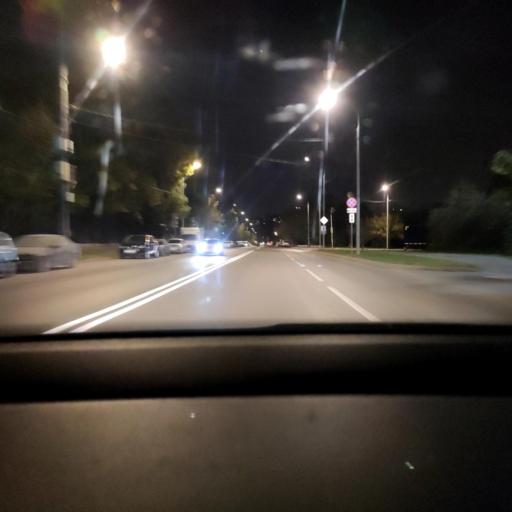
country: RU
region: Moscow
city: Vagonoremont
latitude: 55.8996
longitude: 37.5288
